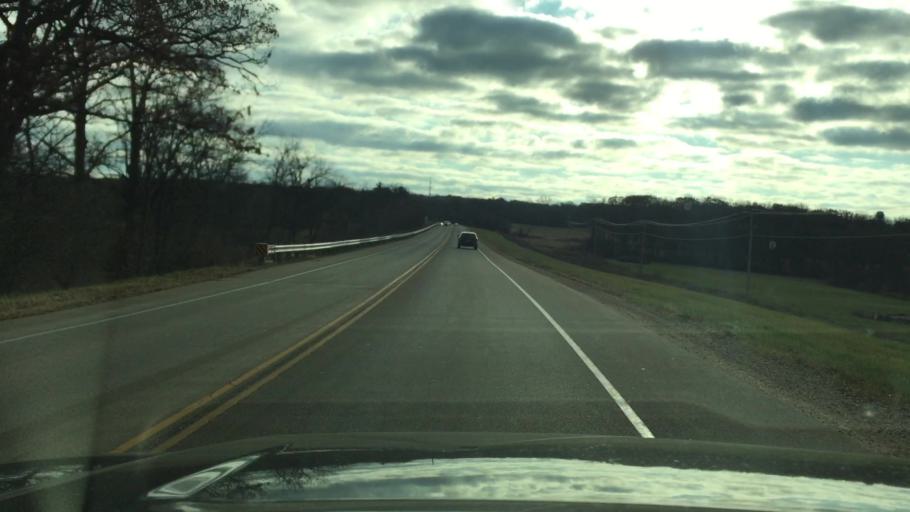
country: US
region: Wisconsin
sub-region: Walworth County
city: Williams Bay
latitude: 42.5865
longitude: -88.5294
